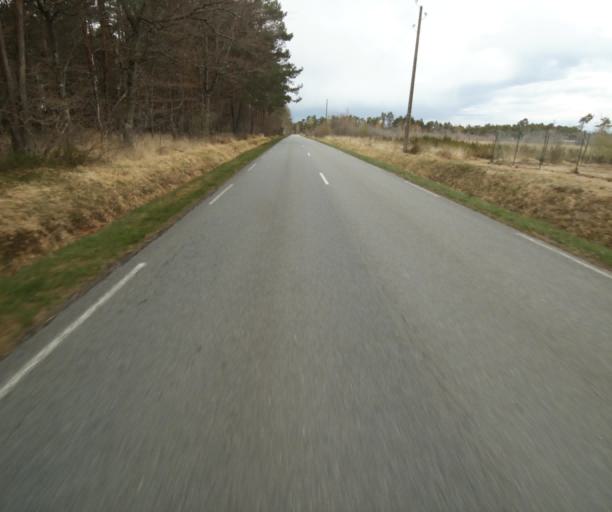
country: FR
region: Limousin
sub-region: Departement de la Correze
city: Saint-Privat
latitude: 45.2067
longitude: 2.0043
